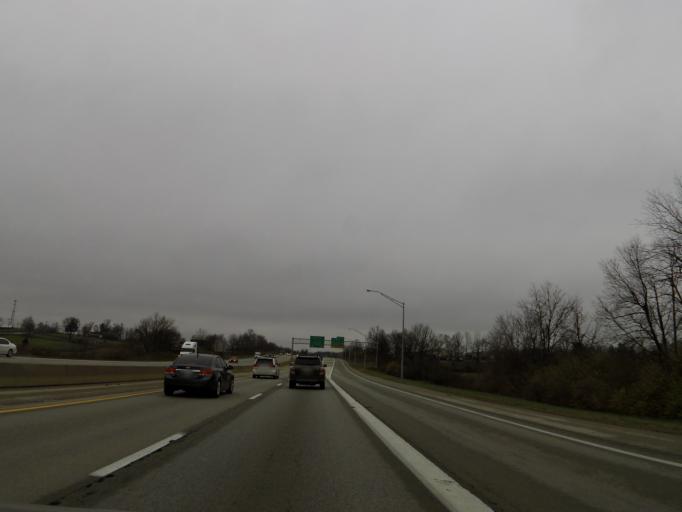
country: US
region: Kentucky
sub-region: Scott County
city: Georgetown
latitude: 38.1260
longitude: -84.5281
